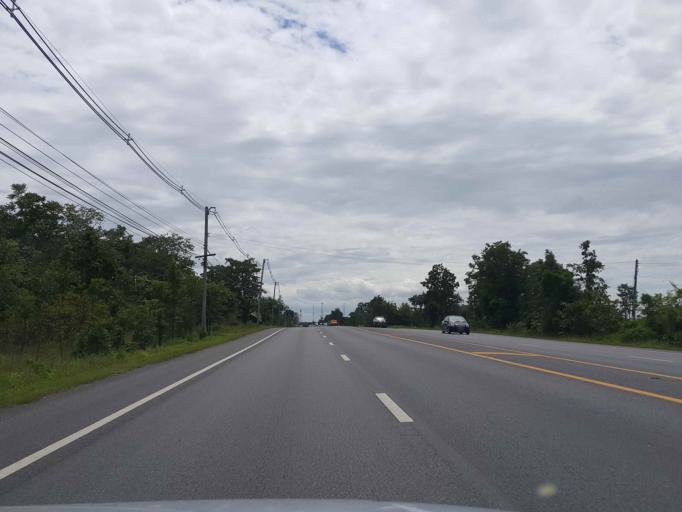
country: TH
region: Sukhothai
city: Ban Dan Lan Hoi
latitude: 16.9519
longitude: 99.4428
